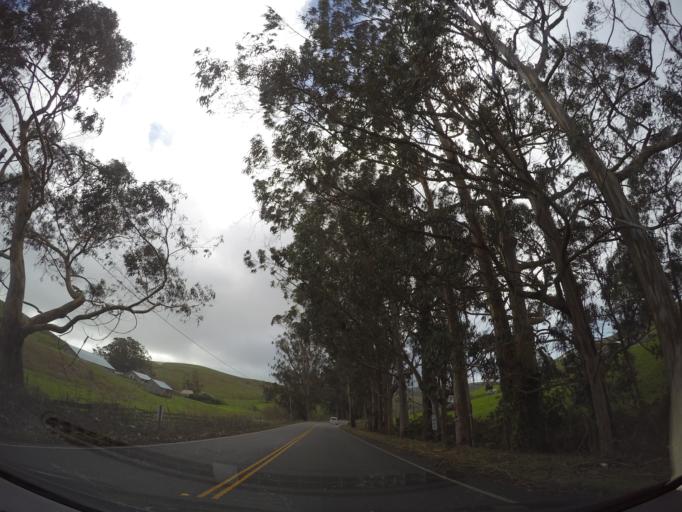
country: US
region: California
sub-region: Sonoma County
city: Bodega Bay
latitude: 38.3325
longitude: -122.9947
